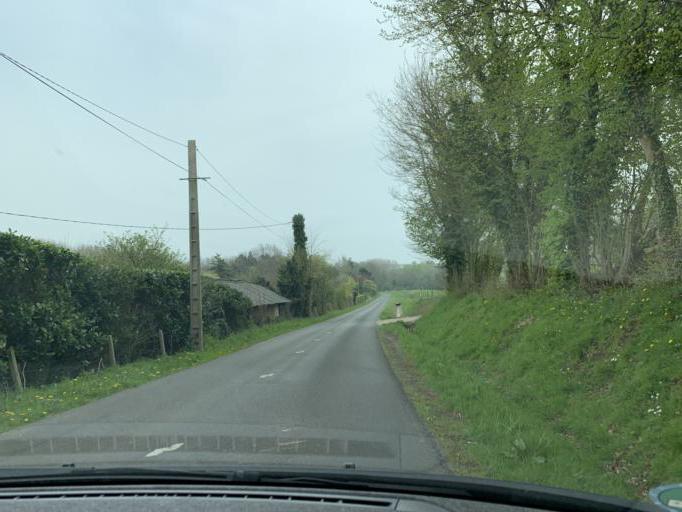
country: FR
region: Haute-Normandie
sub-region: Departement de la Seine-Maritime
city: Saint-Valery-en-Caux
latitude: 49.8568
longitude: 0.7233
